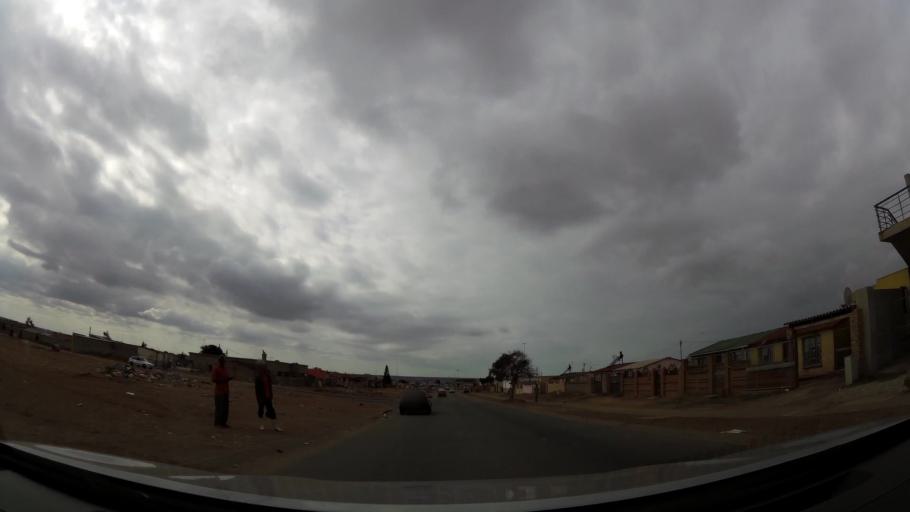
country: ZA
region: Eastern Cape
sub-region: Nelson Mandela Bay Metropolitan Municipality
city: Port Elizabeth
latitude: -33.8685
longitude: 25.5673
